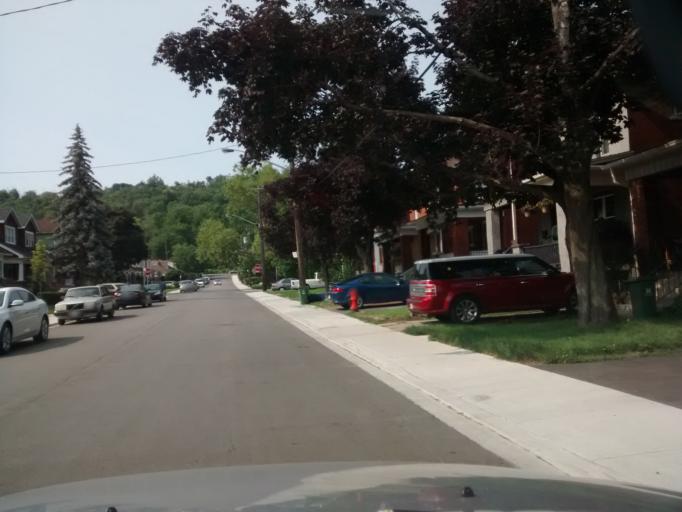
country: CA
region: Ontario
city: Hamilton
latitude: 43.2368
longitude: -79.8221
